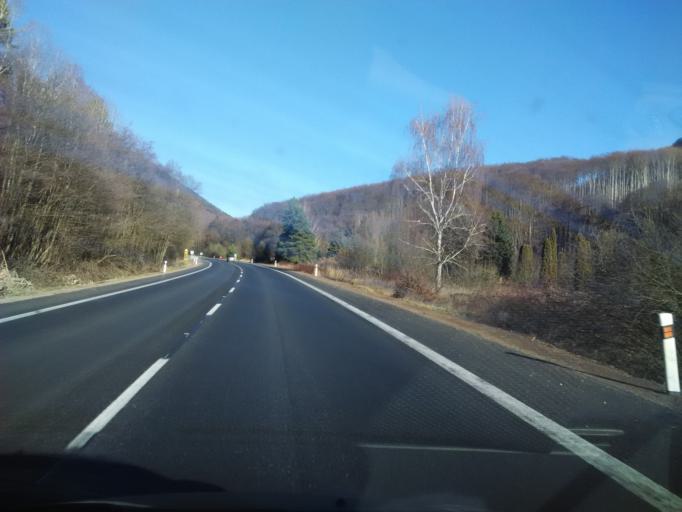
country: SK
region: Banskobystricky
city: Ziar nad Hronom
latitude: 48.6319
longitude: 18.9018
